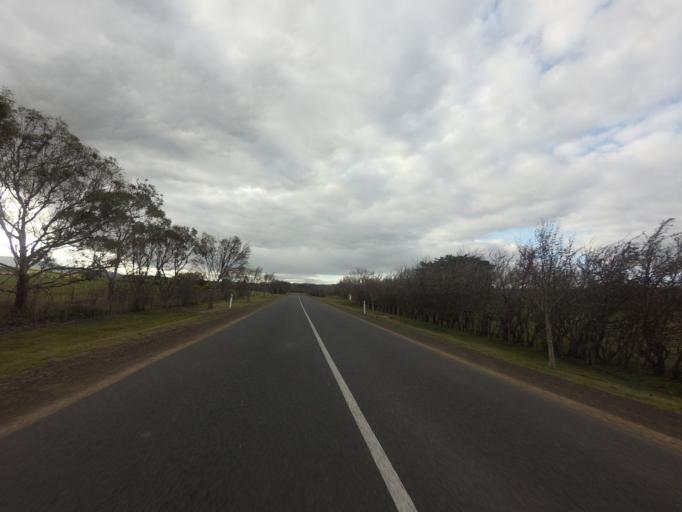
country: AU
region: Tasmania
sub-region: Northern Midlands
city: Evandale
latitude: -42.0193
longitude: 147.4920
